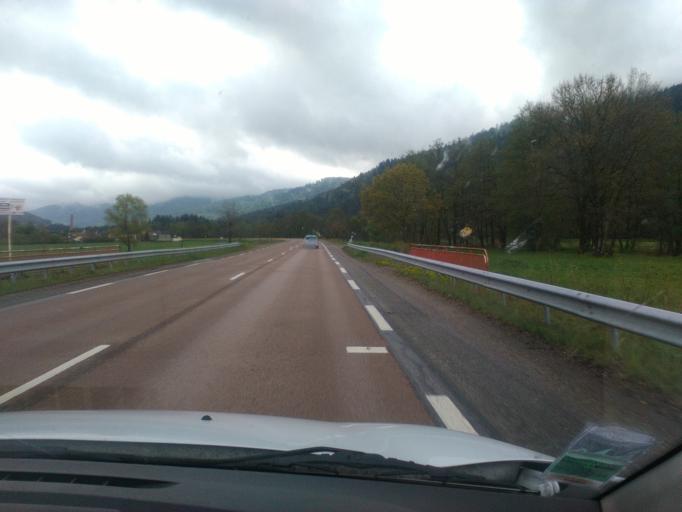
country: FR
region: Lorraine
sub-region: Departement des Vosges
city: Vagney
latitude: 48.0002
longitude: 6.7118
